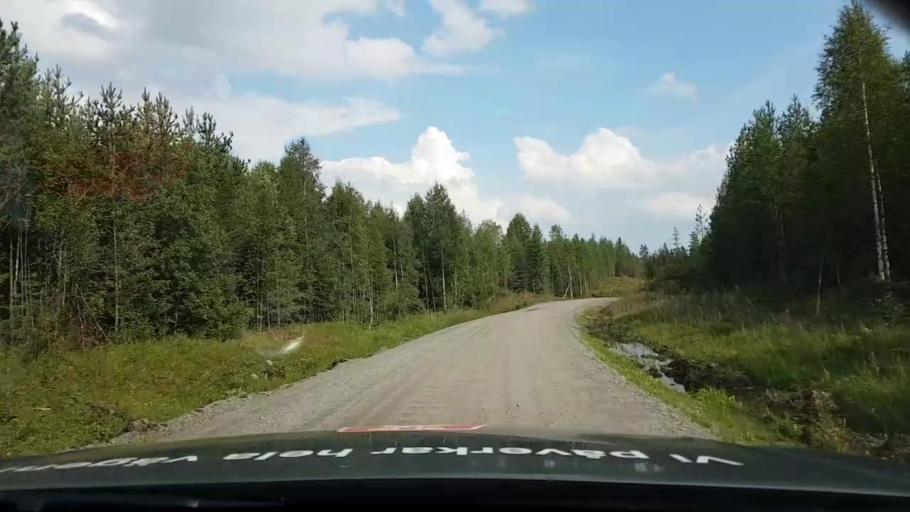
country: SE
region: Vaesternorrland
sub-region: Ange Kommun
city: Fransta
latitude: 62.7768
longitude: 15.9687
